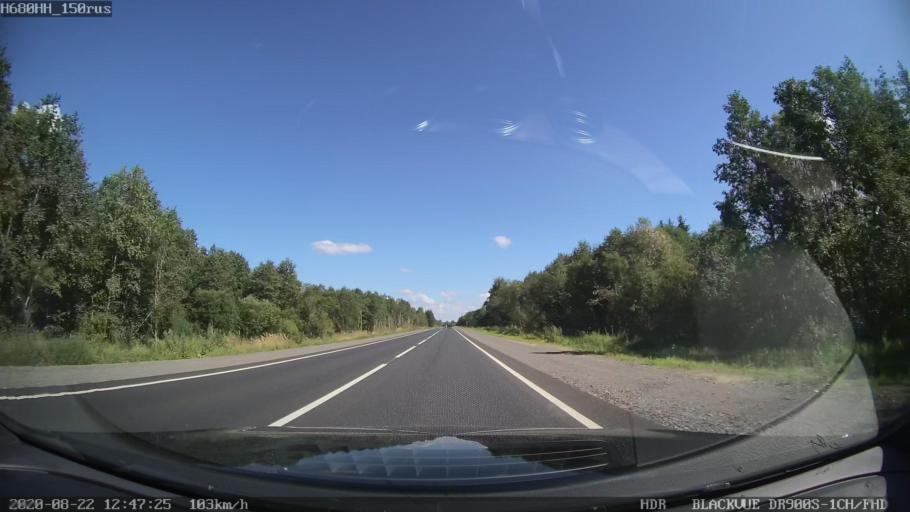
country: RU
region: Tverskaya
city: Rameshki
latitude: 57.4294
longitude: 36.1662
